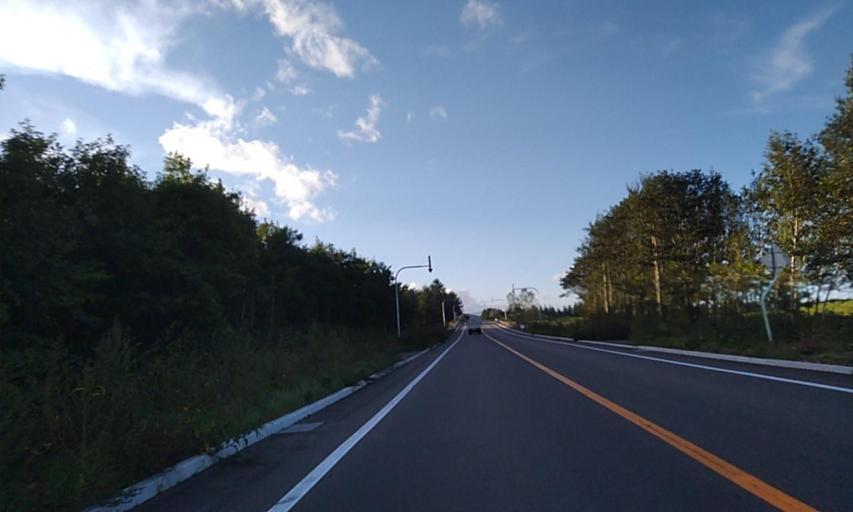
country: JP
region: Hokkaido
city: Otofuke
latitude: 42.9786
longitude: 142.8653
